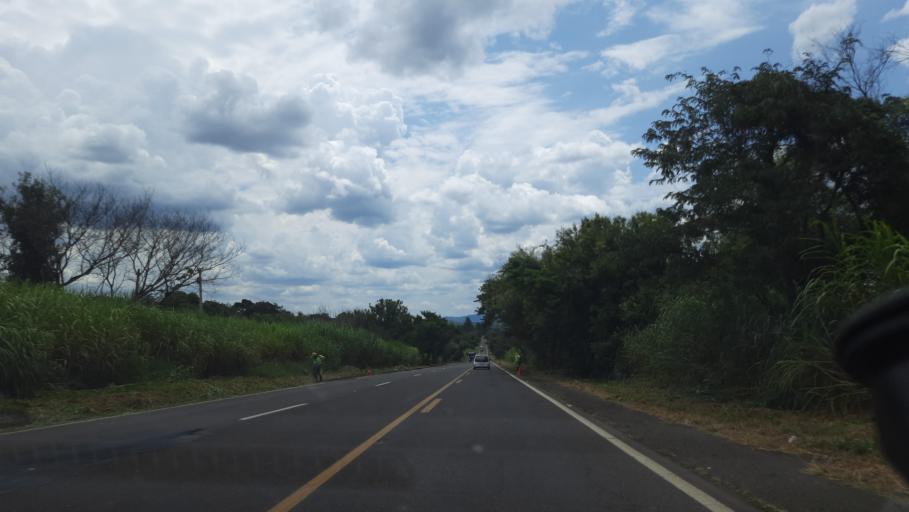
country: BR
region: Sao Paulo
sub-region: Mococa
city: Mococa
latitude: -21.4775
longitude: -47.0880
